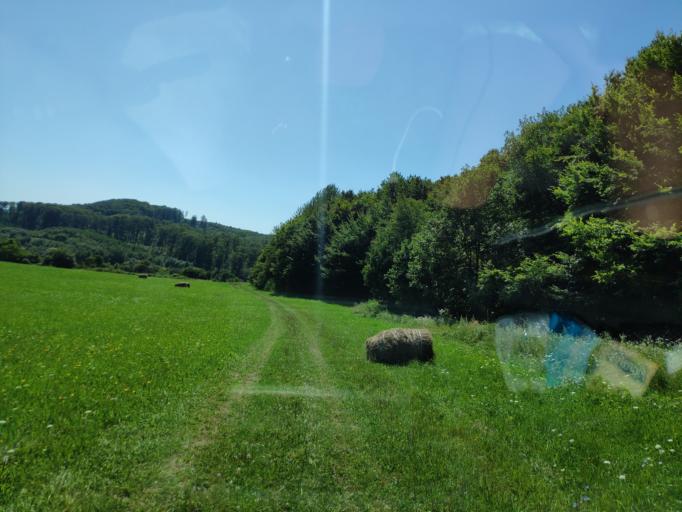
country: SK
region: Kosicky
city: Kosice
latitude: 48.6351
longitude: 21.4571
